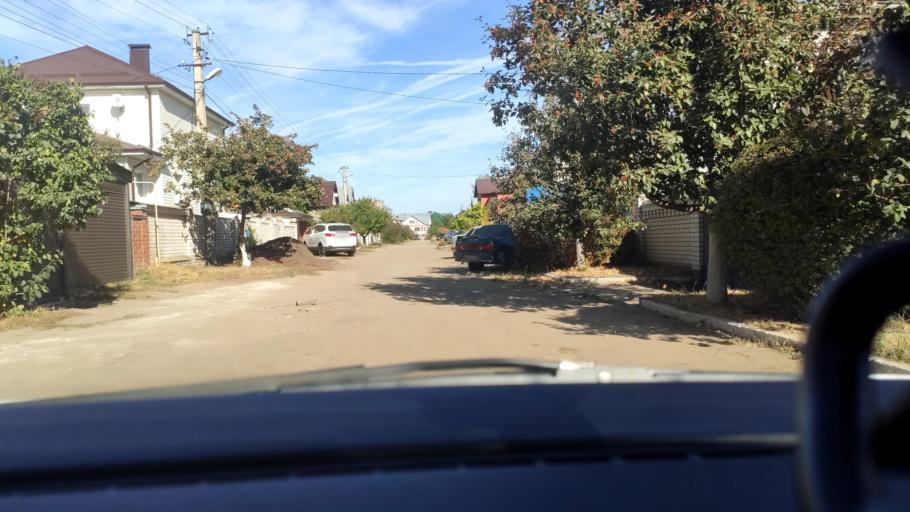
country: RU
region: Voronezj
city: Pridonskoy
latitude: 51.6413
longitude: 39.0839
